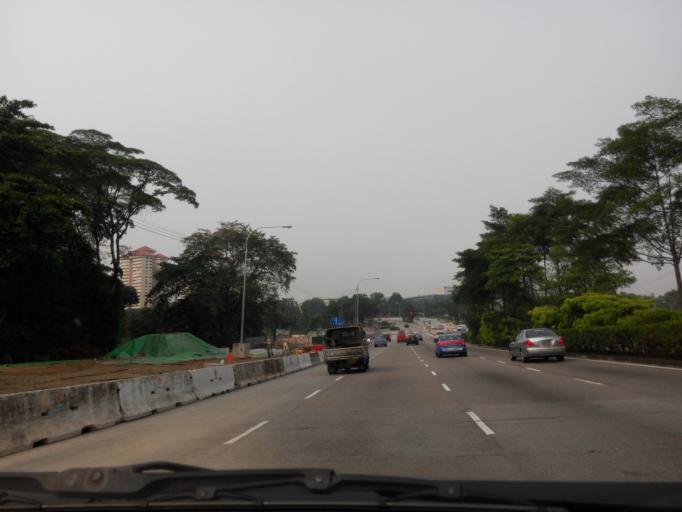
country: SG
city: Singapore
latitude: 1.2912
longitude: 103.7967
